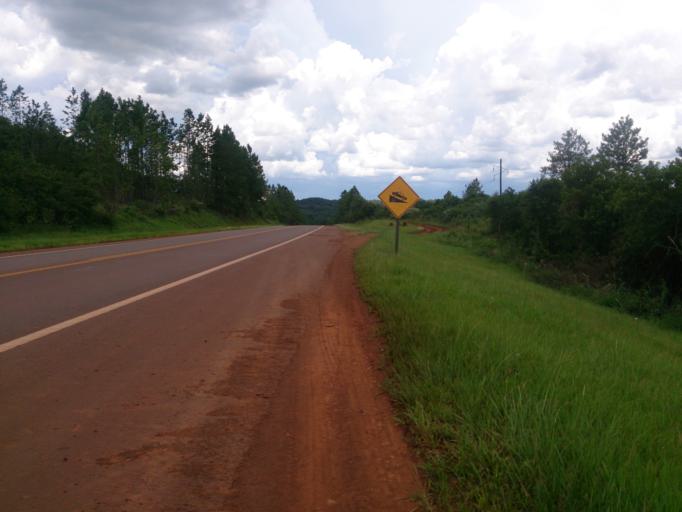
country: AR
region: Misiones
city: Campo Viera
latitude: -27.3599
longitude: -55.0505
